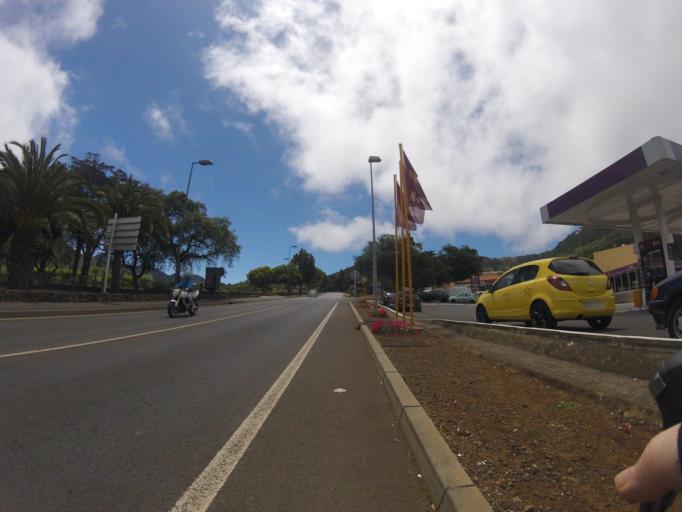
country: ES
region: Canary Islands
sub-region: Provincia de Santa Cruz de Tenerife
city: Tegueste
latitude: 28.5201
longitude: -16.3350
